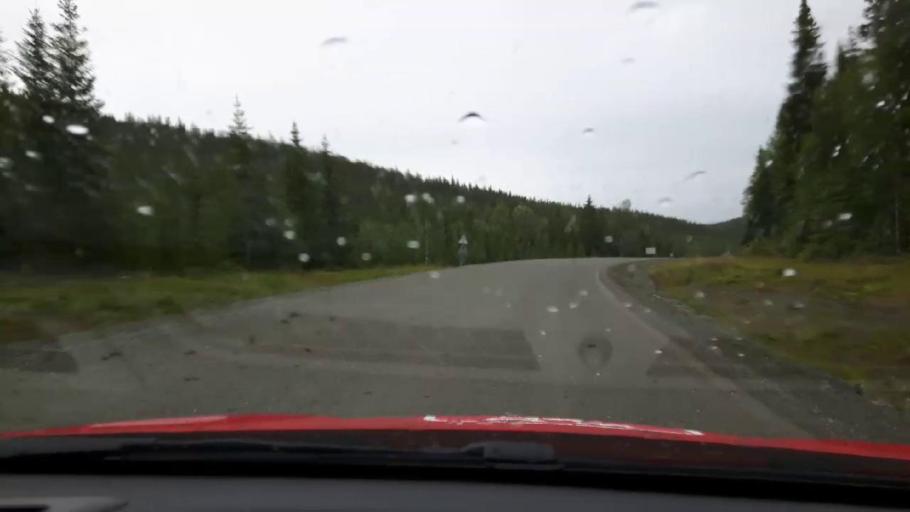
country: SE
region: Jaemtland
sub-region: Are Kommun
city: Are
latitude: 63.4310
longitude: 12.7356
